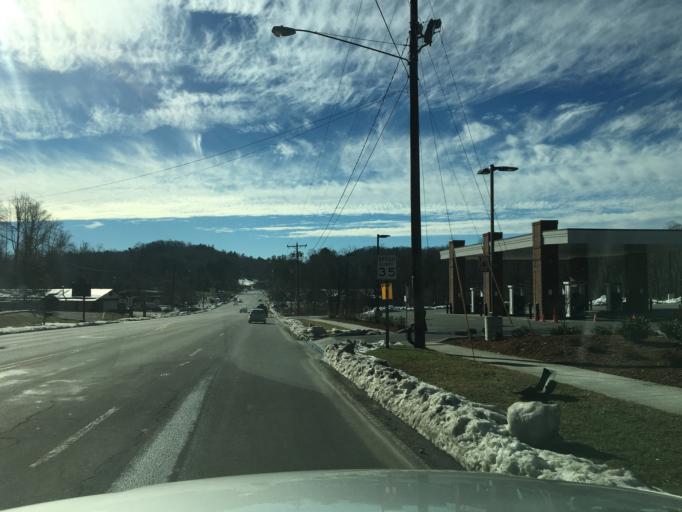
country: US
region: North Carolina
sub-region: Transylvania County
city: Brevard
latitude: 35.2261
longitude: -82.7384
